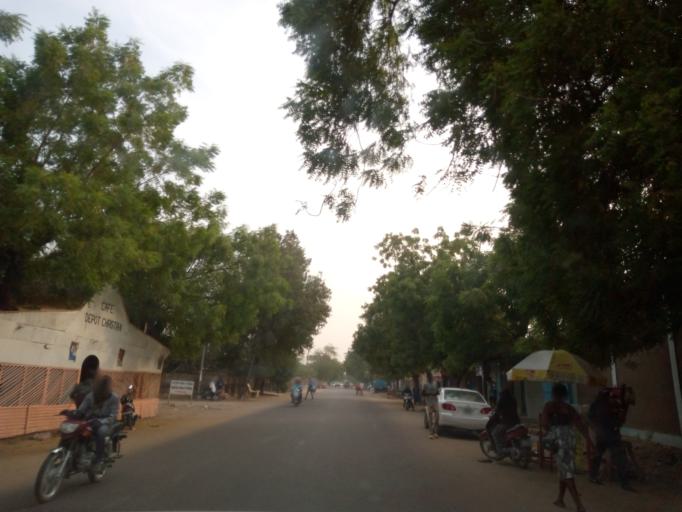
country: TD
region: Chari-Baguirmi
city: N'Djamena
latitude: 12.1062
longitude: 15.0751
